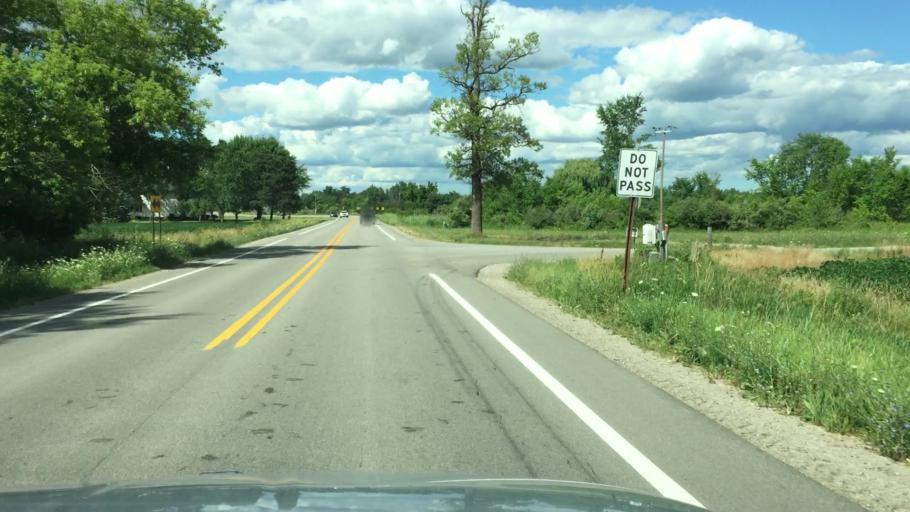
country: US
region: Michigan
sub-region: Saint Clair County
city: Capac
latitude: 42.9802
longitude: -82.9288
